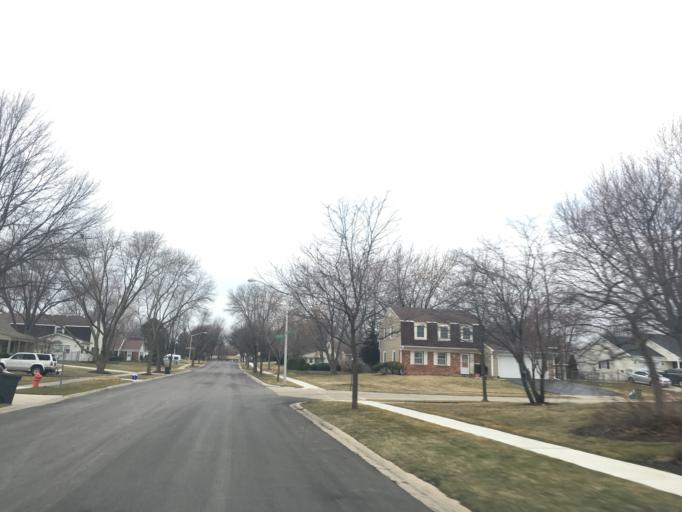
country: US
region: Illinois
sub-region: DuPage County
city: Hanover Park
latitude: 42.0272
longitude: -88.1205
